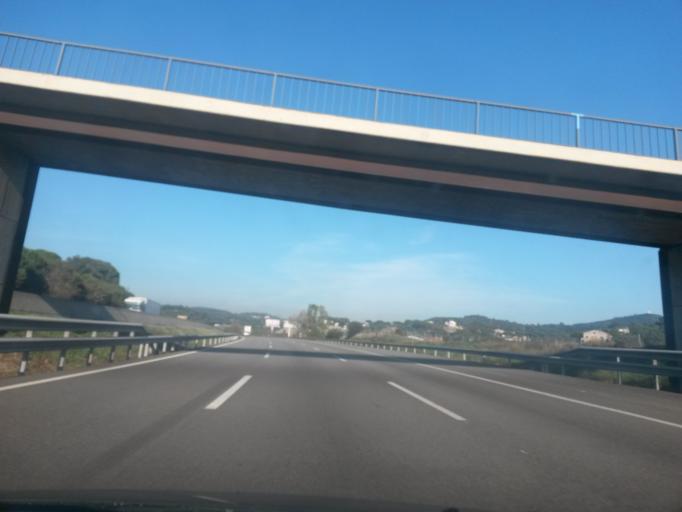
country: ES
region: Catalonia
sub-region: Provincia de Girona
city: Macanet de la Selva
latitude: 41.7521
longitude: 2.7075
